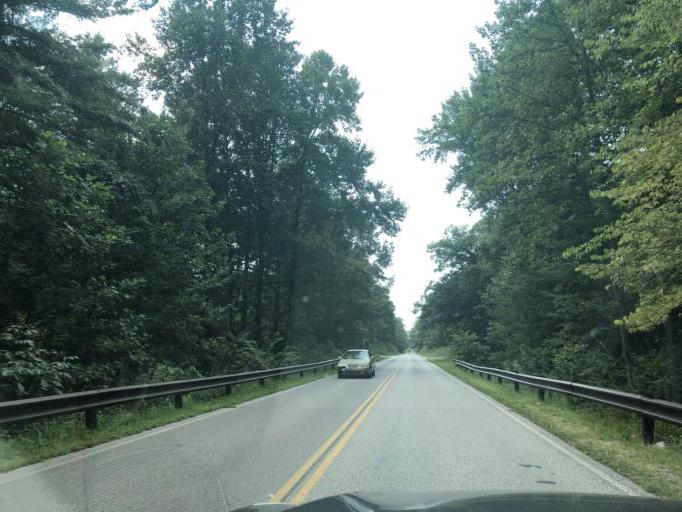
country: US
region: Tennessee
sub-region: Franklin County
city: Sewanee
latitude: 35.2077
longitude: -85.9075
